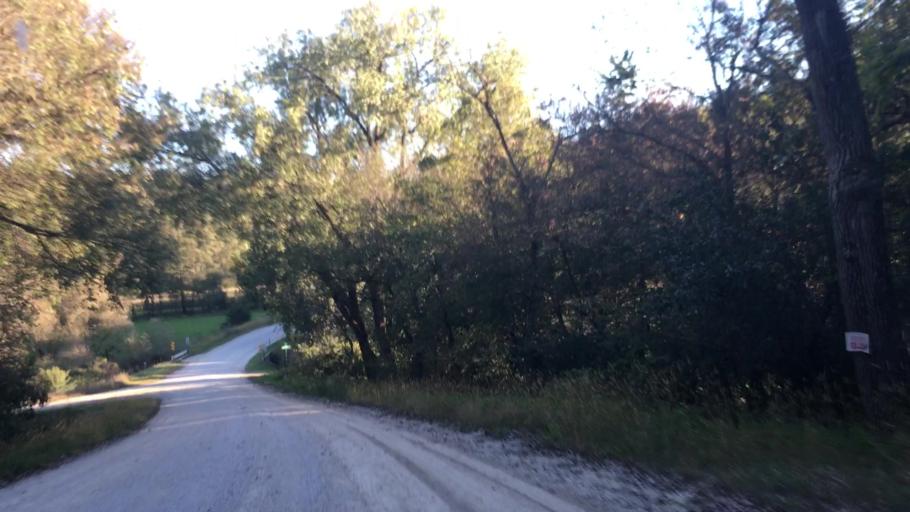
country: US
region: Minnesota
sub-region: Fillmore County
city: Preston
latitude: 43.7633
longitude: -92.0295
